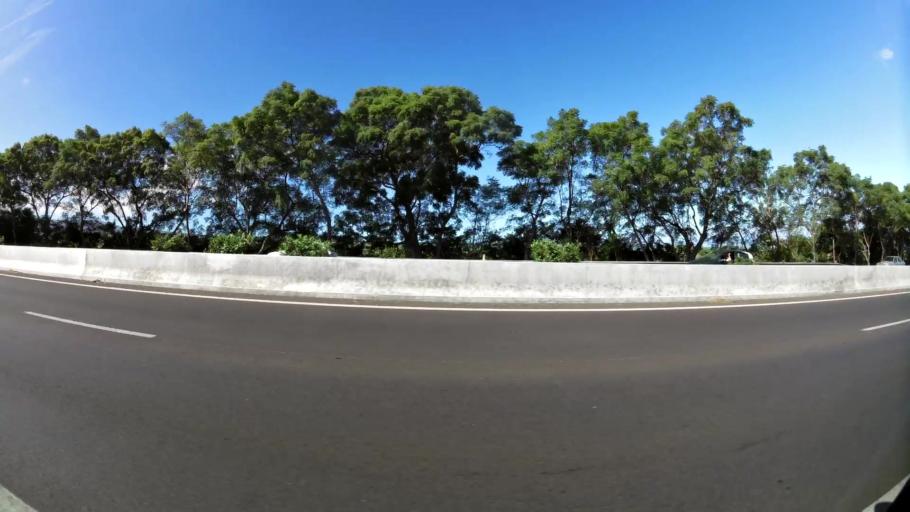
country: RE
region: Reunion
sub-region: Reunion
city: Le Tampon
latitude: -21.2925
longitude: 55.5125
